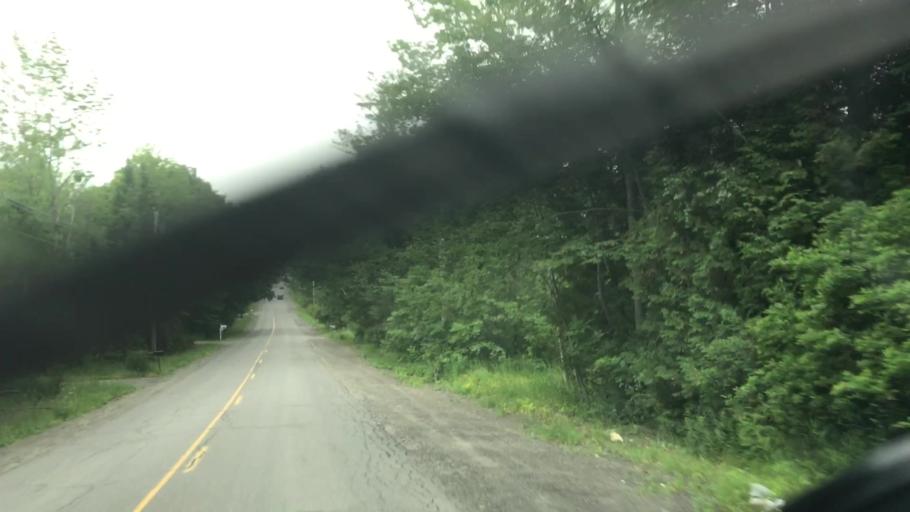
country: US
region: Maine
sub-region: Penobscot County
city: Veazie
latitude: 44.8759
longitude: -68.7133
